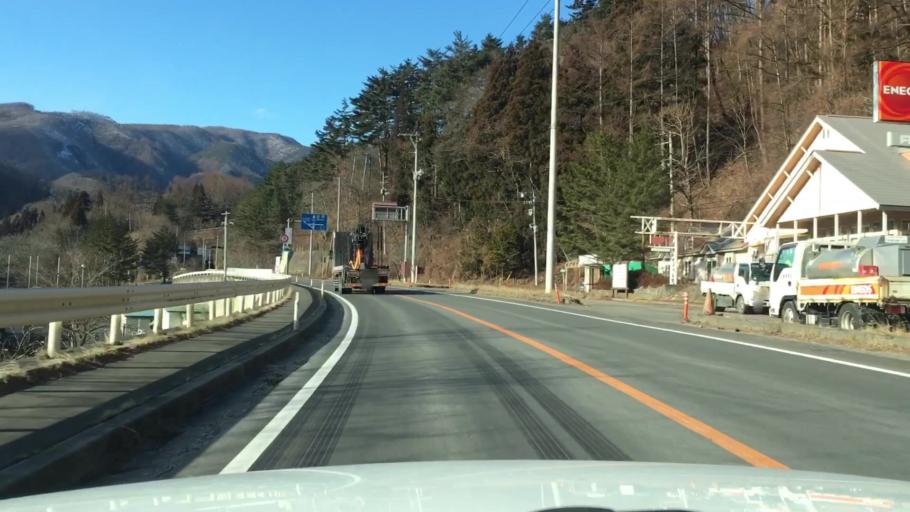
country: JP
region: Iwate
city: Tono
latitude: 39.6407
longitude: 141.5998
